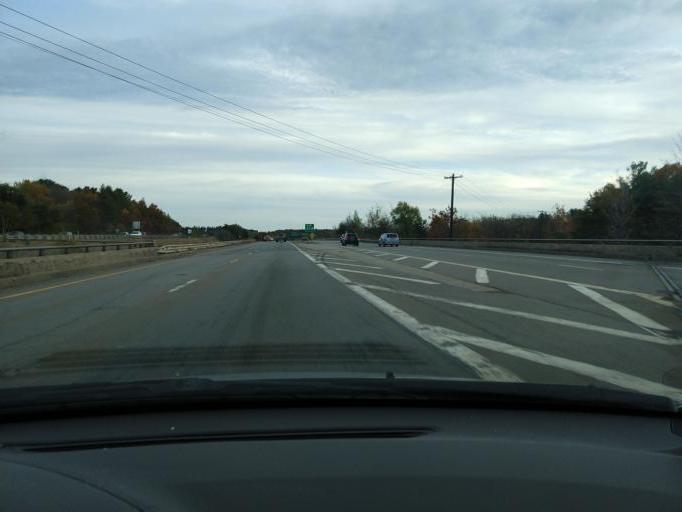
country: US
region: Massachusetts
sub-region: Worcester County
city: Leominster
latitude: 42.5291
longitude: -71.7344
